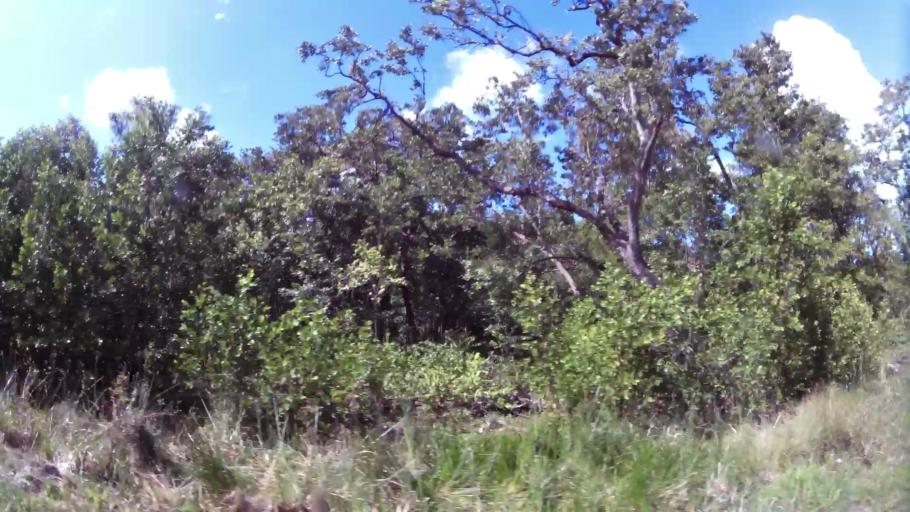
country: DM
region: Saint John
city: Portsmouth
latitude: 15.5857
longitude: -61.4642
